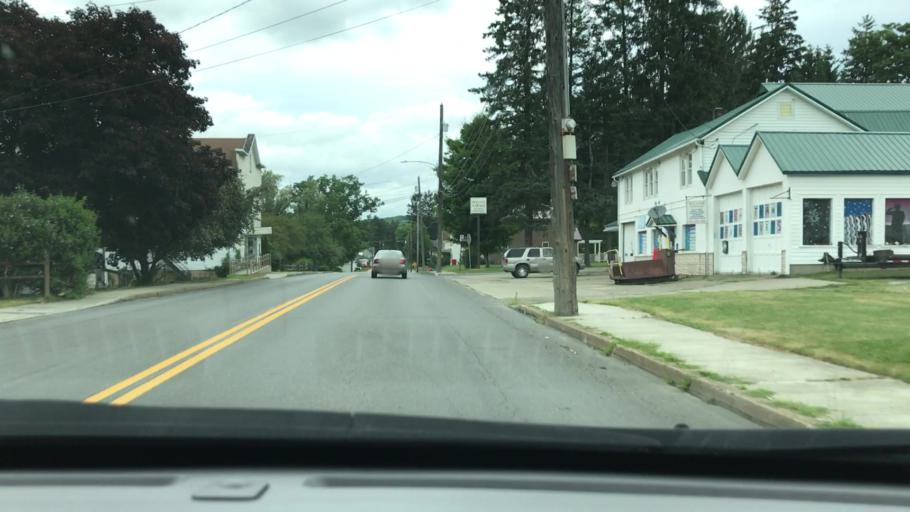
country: US
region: Pennsylvania
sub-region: Elk County
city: Johnsonburg
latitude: 41.5758
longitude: -78.6884
